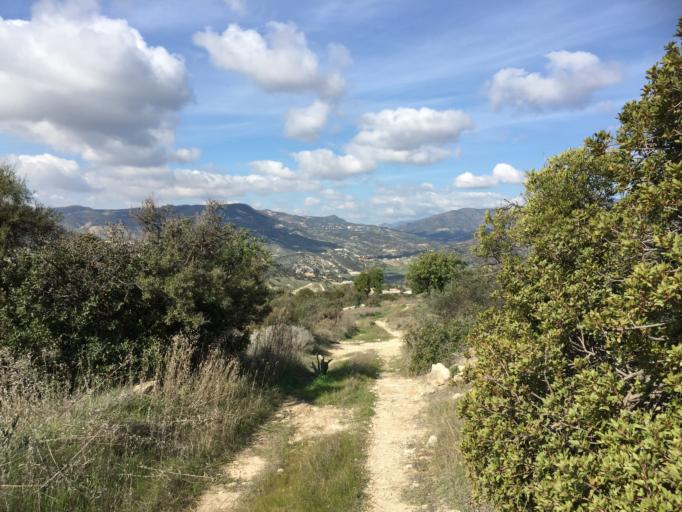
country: CY
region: Limassol
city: Mouttagiaka
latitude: 34.7465
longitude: 33.1146
